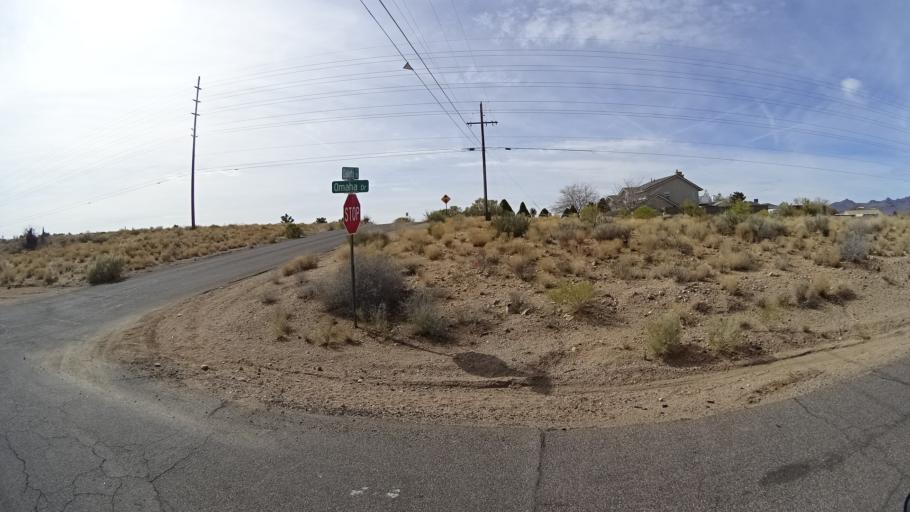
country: US
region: Arizona
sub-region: Mohave County
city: Kingman
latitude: 35.1882
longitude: -113.9843
